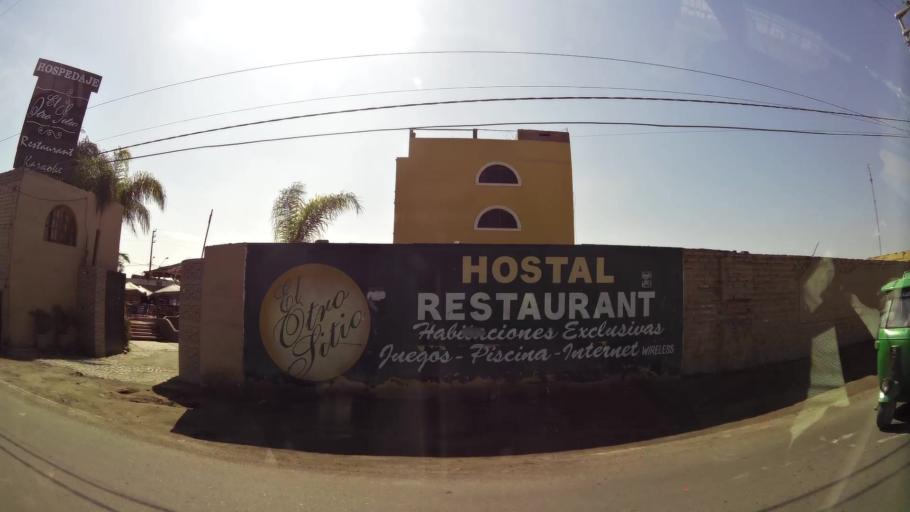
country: PE
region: Ica
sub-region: Provincia de Chincha
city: Sunampe
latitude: -13.4172
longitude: -76.1574
